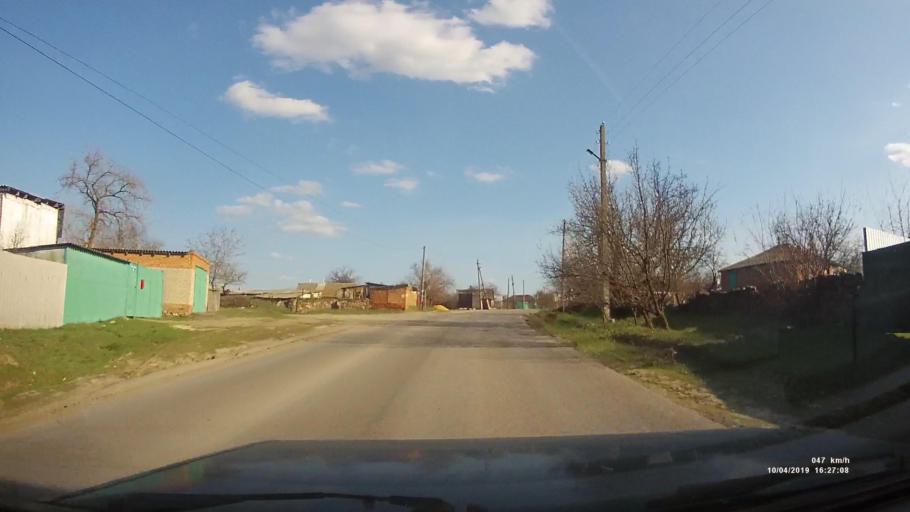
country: RU
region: Rostov
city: Staraya Stanitsa
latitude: 48.2867
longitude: 40.3415
